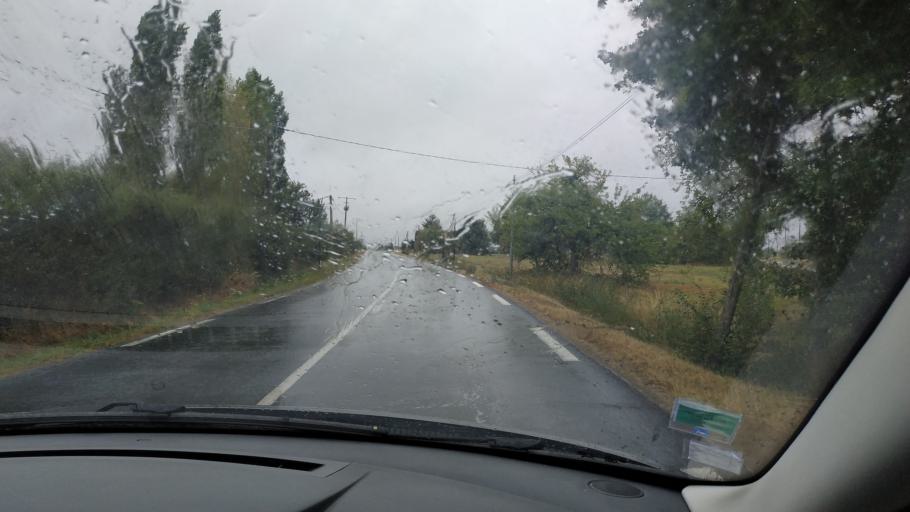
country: FR
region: Centre
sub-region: Departement du Loiret
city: Bellegarde
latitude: 47.9216
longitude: 2.3964
